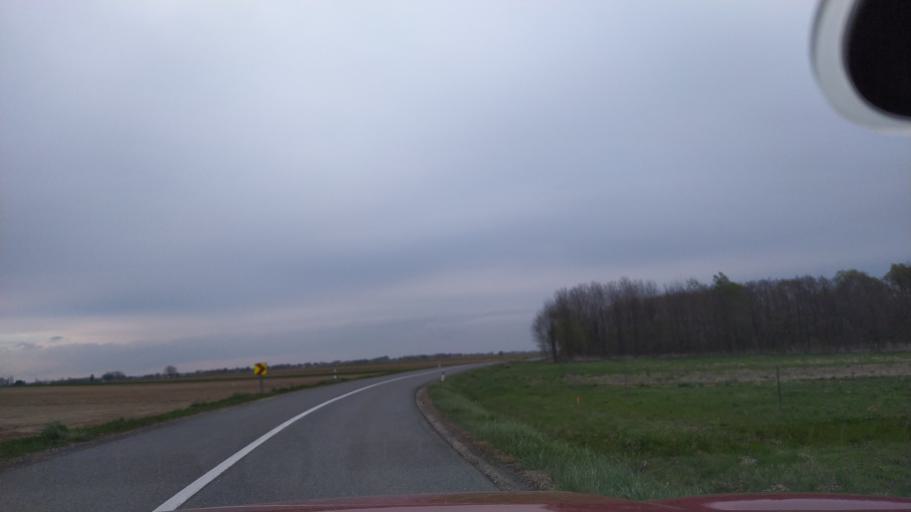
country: HR
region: Varazdinska
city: Ludbreg
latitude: 46.2489
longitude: 16.5611
